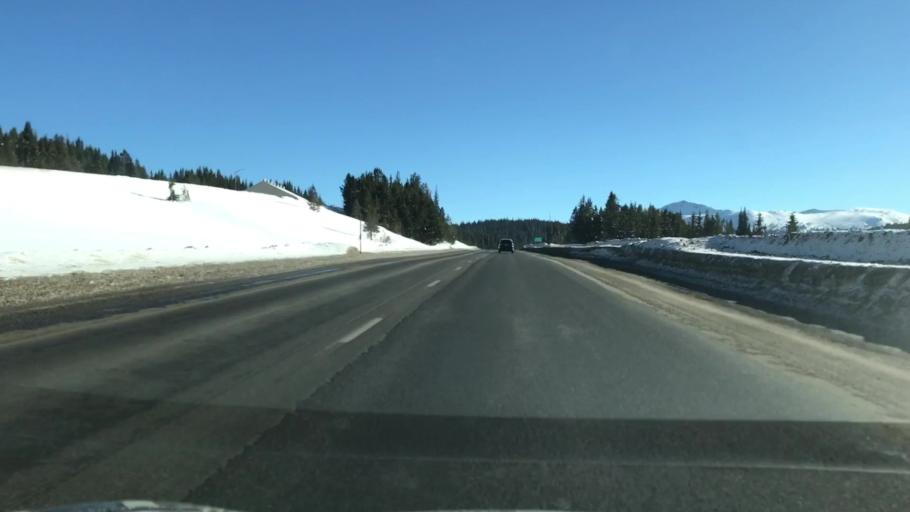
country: US
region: Colorado
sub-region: Summit County
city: Frisco
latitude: 39.5442
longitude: -106.2186
